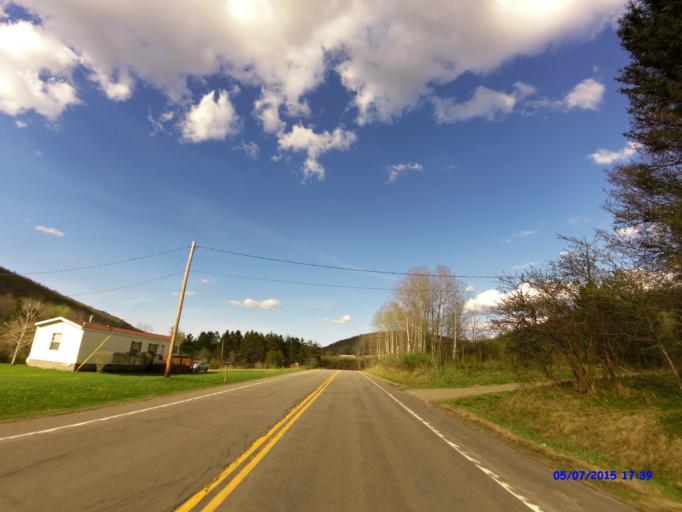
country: US
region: New York
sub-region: Cattaraugus County
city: Franklinville
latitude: 42.2621
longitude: -78.5488
